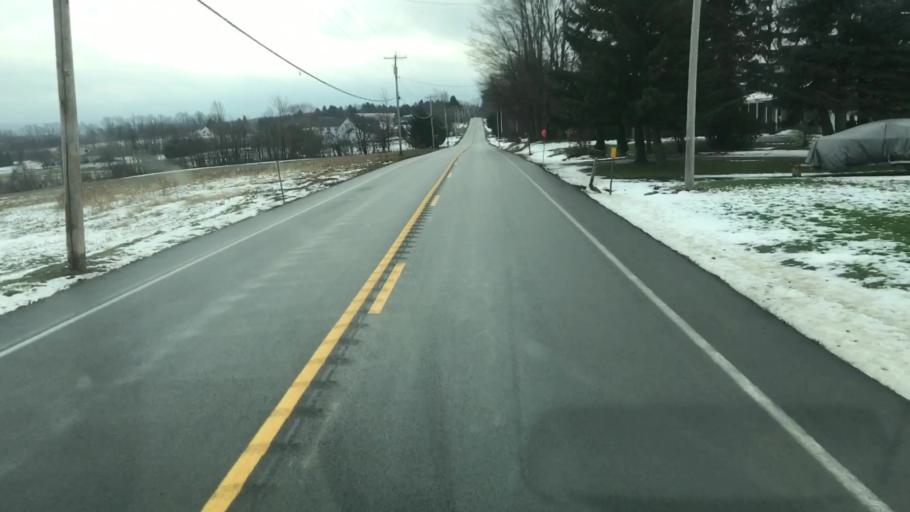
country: US
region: New York
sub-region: Onondaga County
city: Skaneateles
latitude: 42.8453
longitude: -76.3872
